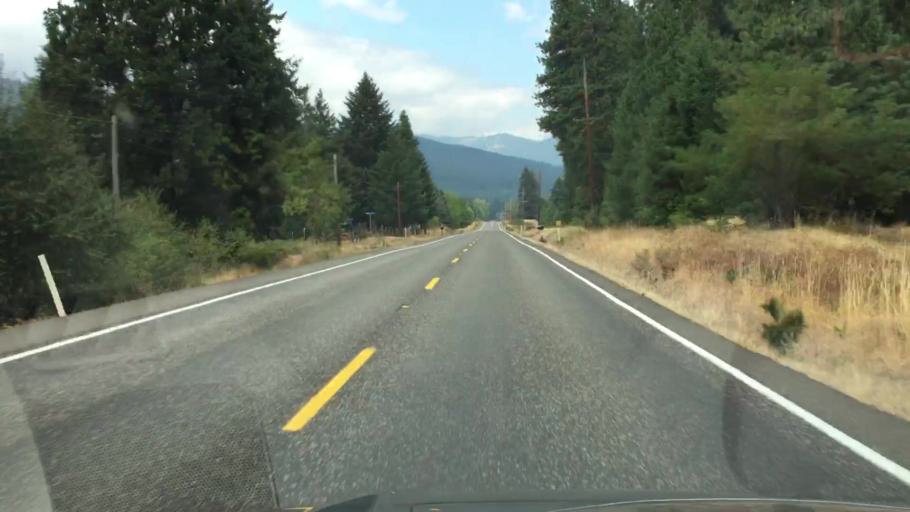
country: US
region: Washington
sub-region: Klickitat County
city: White Salmon
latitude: 45.8367
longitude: -121.4989
